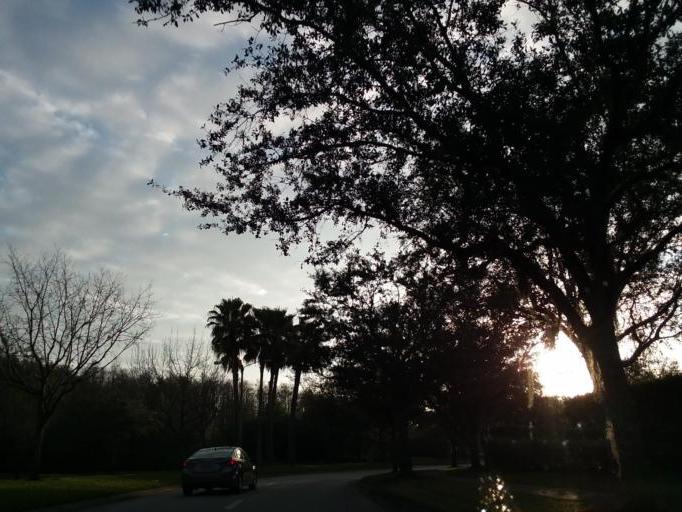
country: US
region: Florida
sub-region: Osceola County
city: Campbell
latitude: 28.2267
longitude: -81.4413
